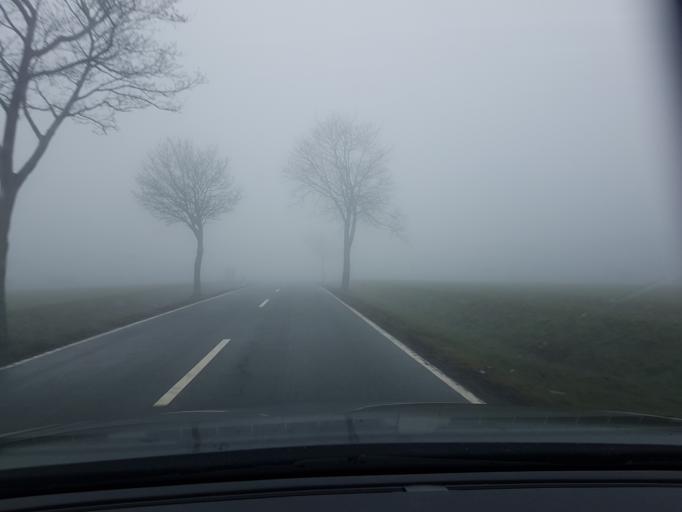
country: DE
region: Saxony-Anhalt
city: Stolberg
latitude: 51.5720
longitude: 11.0301
